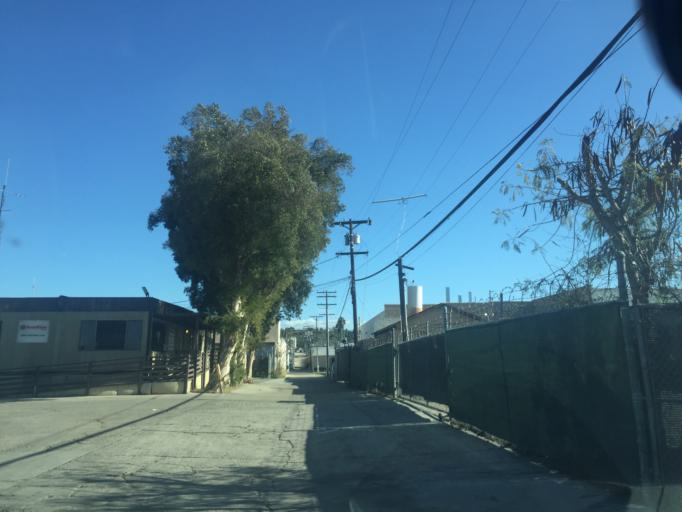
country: US
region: California
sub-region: San Diego County
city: La Mesa
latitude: 32.7882
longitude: -117.1011
